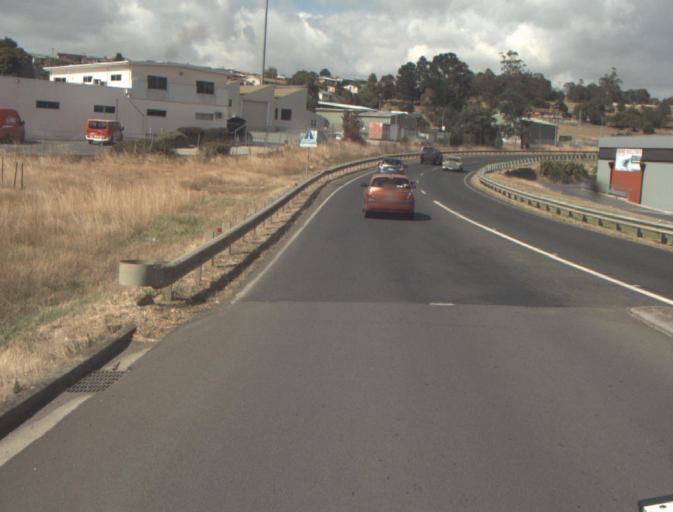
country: AU
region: Tasmania
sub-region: Launceston
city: Summerhill
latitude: -41.4766
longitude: 147.1644
